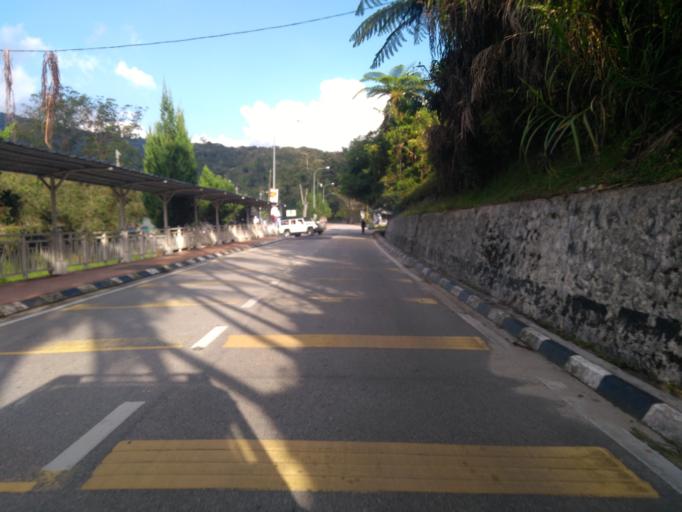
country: MY
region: Pahang
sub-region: Cameron Highlands
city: Tanah Rata
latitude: 4.4678
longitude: 101.3838
